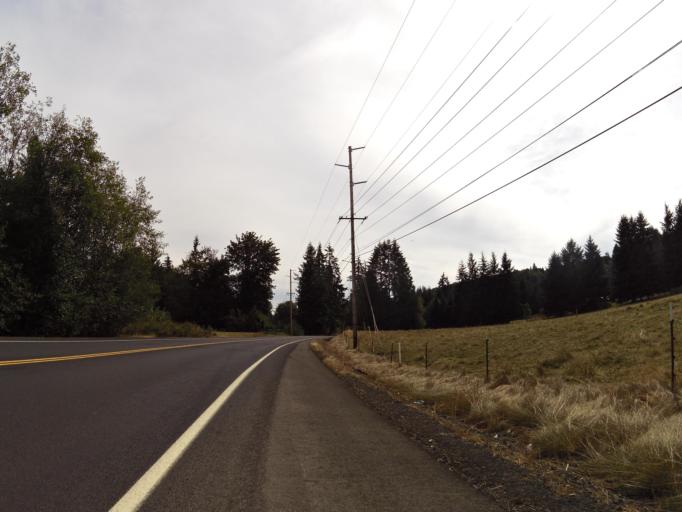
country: US
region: Washington
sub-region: Cowlitz County
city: Castle Rock
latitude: 46.3270
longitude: -122.9287
